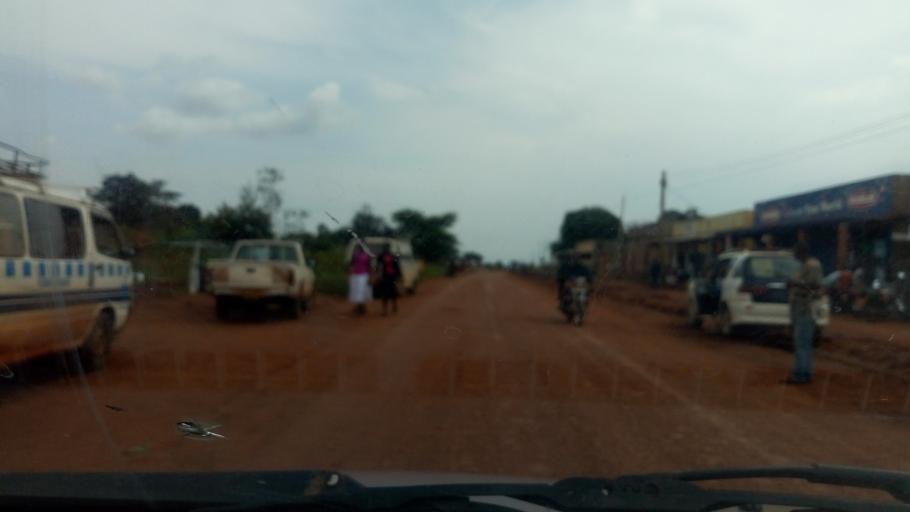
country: UG
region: Western Region
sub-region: Kiryandongo District
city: Kiryandongo
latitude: 1.8090
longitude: 32.0072
